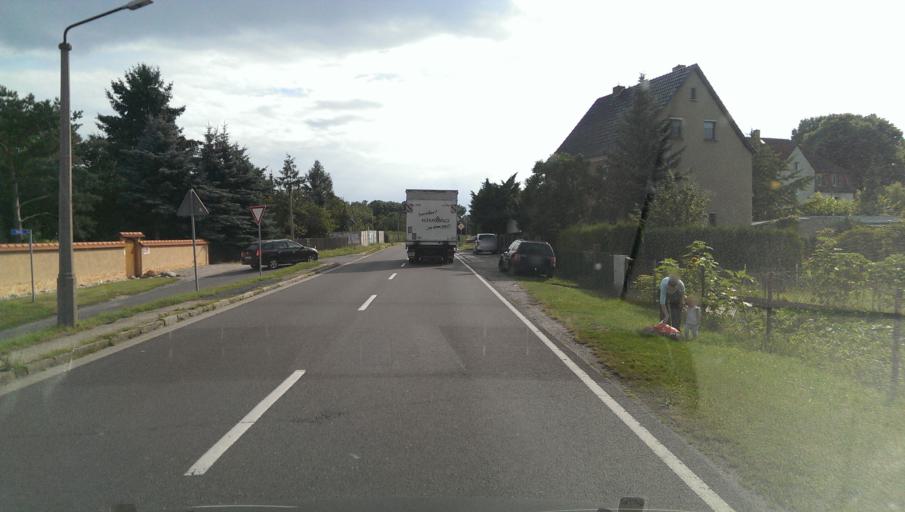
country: DE
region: Saxony
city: Elstertrebnitz
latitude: 51.1293
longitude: 12.2170
